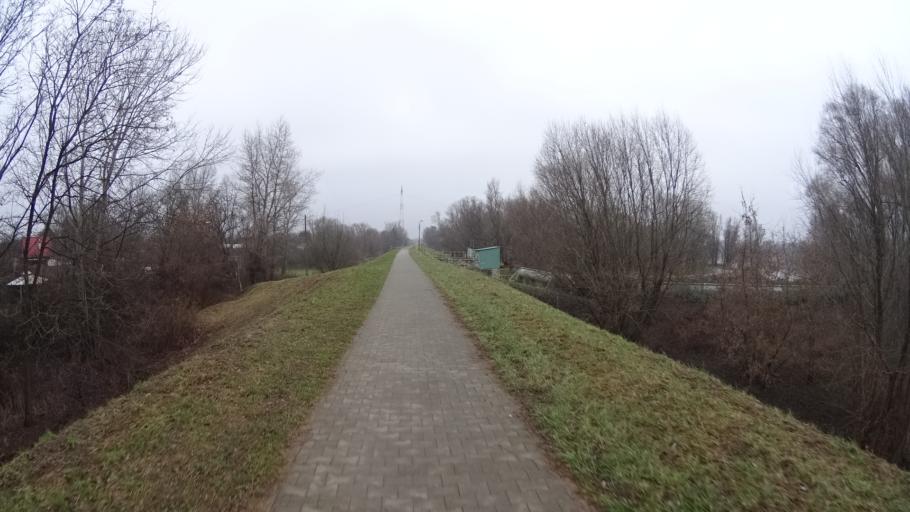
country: PL
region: Masovian Voivodeship
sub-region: Warszawa
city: Wilanow
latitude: 52.1923
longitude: 21.1019
